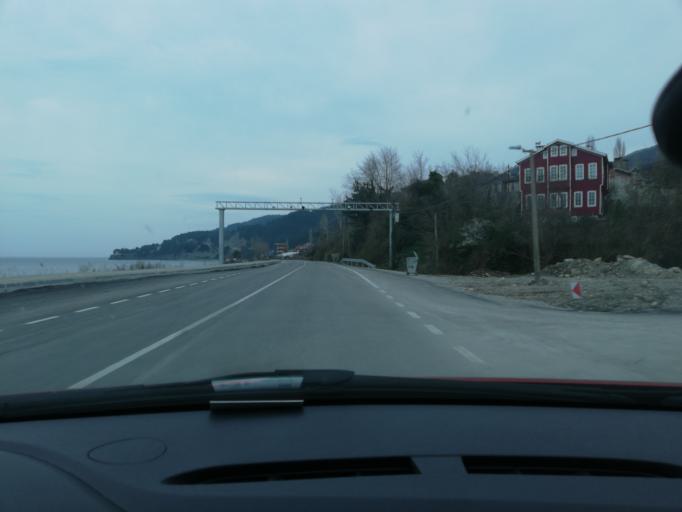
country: TR
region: Kastamonu
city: Inebolu
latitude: 41.9751
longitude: 33.7732
